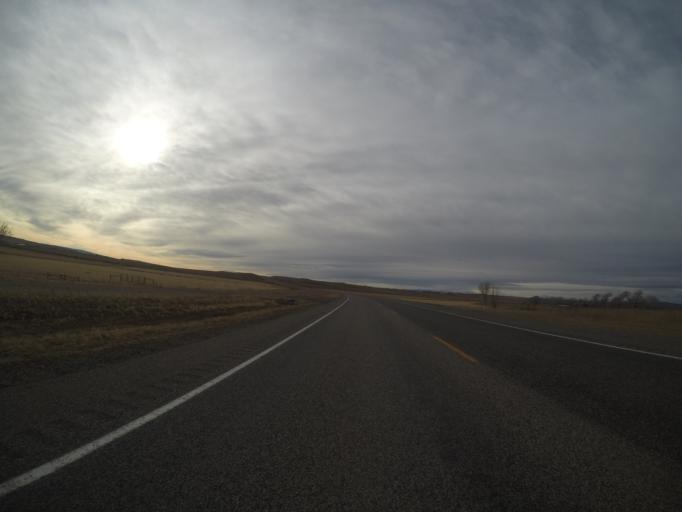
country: US
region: Montana
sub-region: Yellowstone County
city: Laurel
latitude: 45.6132
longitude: -108.8199
